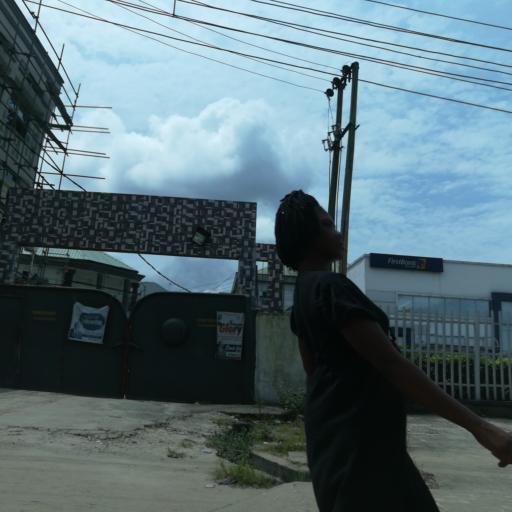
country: NG
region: Rivers
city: Port Harcourt
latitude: 4.7846
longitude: 7.0381
